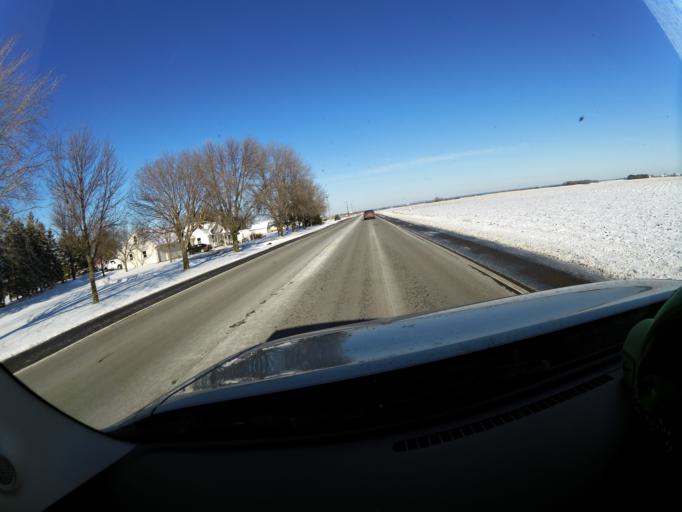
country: US
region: Minnesota
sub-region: Dakota County
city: Hastings
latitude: 44.6669
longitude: -92.9337
